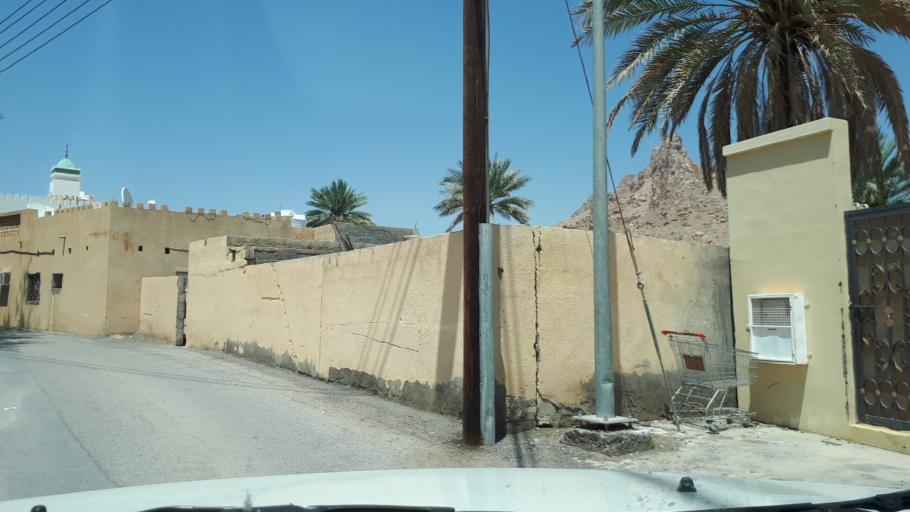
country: OM
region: Muhafazat ad Dakhiliyah
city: Nizwa
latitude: 22.8812
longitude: 57.5265
